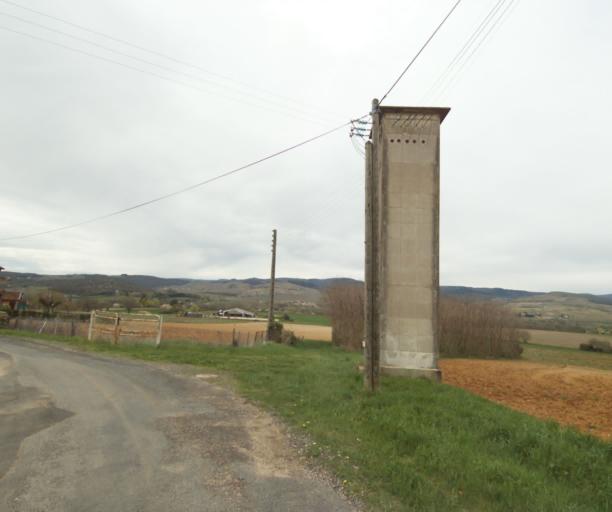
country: FR
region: Bourgogne
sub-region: Departement de Saone-et-Loire
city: Charnay-les-Macon
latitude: 46.3077
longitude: 4.7798
